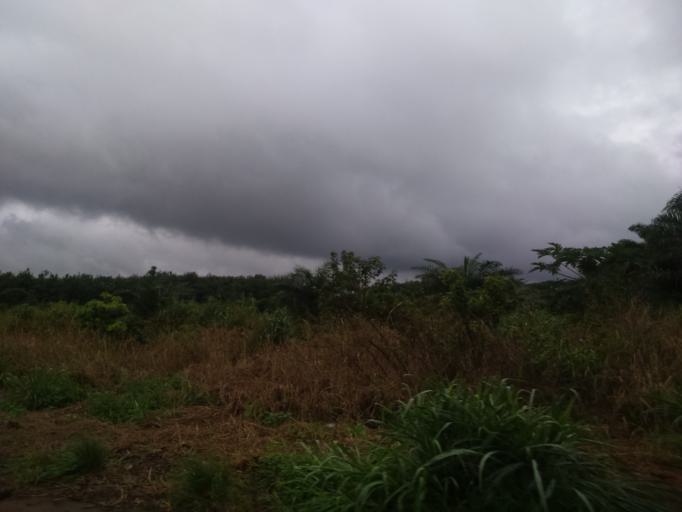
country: CI
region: Sud-Comoe
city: Adiake
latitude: 5.3003
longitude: -3.3482
